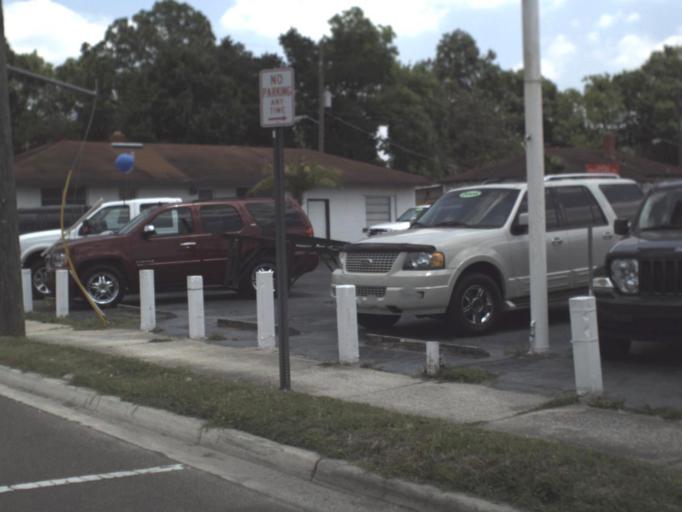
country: US
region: Florida
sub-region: Duval County
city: Jacksonville
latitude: 30.3006
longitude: -81.7304
